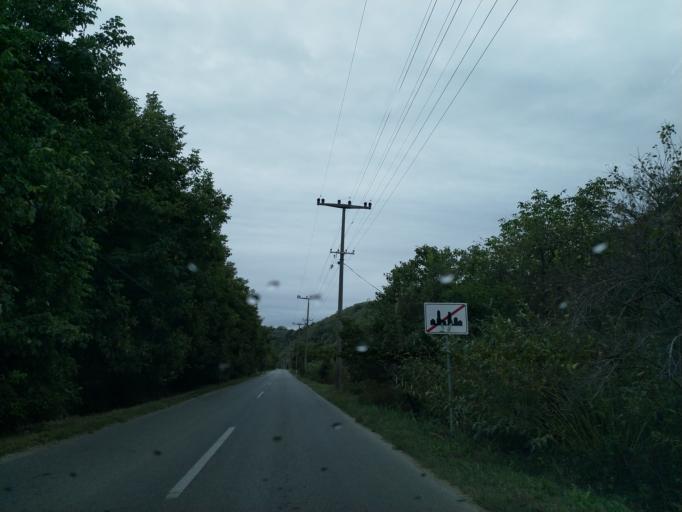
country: RS
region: Central Serbia
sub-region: Sumadijski Okrug
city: Batocina
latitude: 44.1005
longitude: 21.1633
